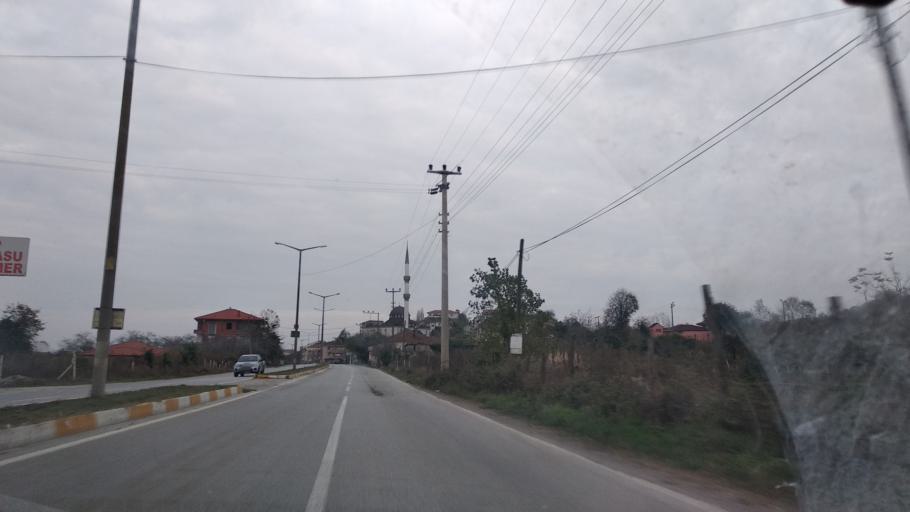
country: TR
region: Sakarya
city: Karasu
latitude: 41.0988
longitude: 30.6721
